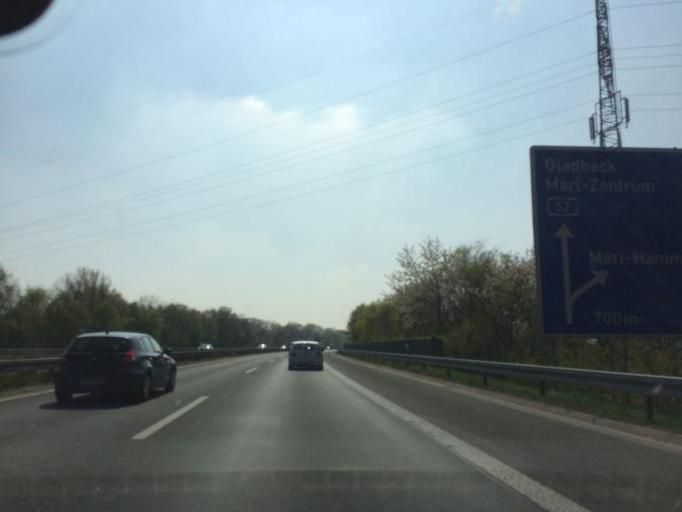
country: DE
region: North Rhine-Westphalia
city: Marl
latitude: 51.6886
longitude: 7.1366
